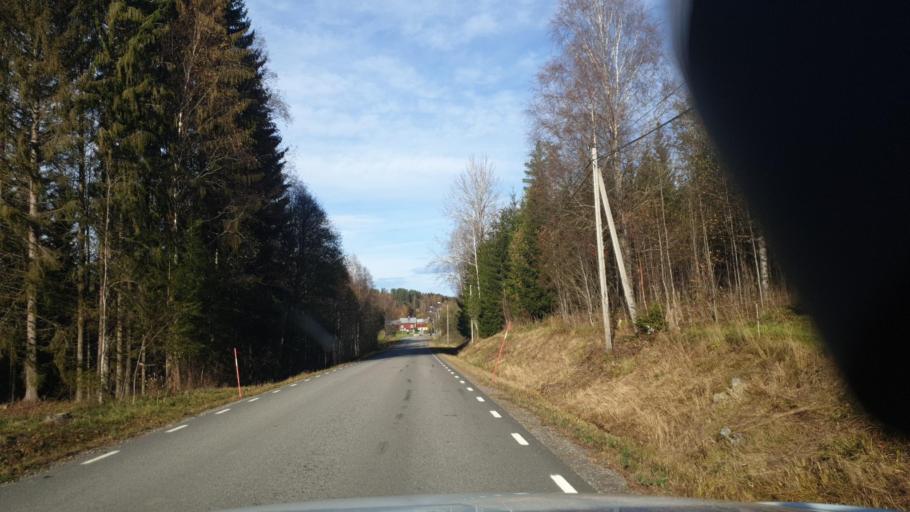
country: SE
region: Vaermland
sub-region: Eda Kommun
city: Charlottenberg
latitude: 59.9271
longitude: 12.5208
